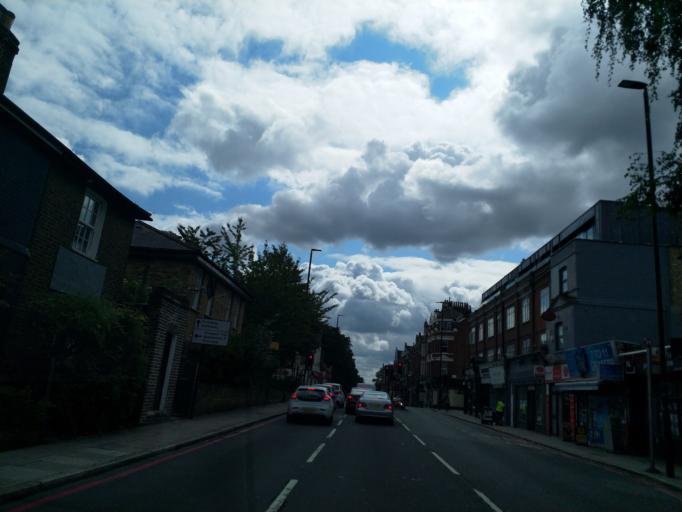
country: GB
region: England
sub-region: Greater London
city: Crouch End
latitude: 51.5781
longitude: -0.1481
